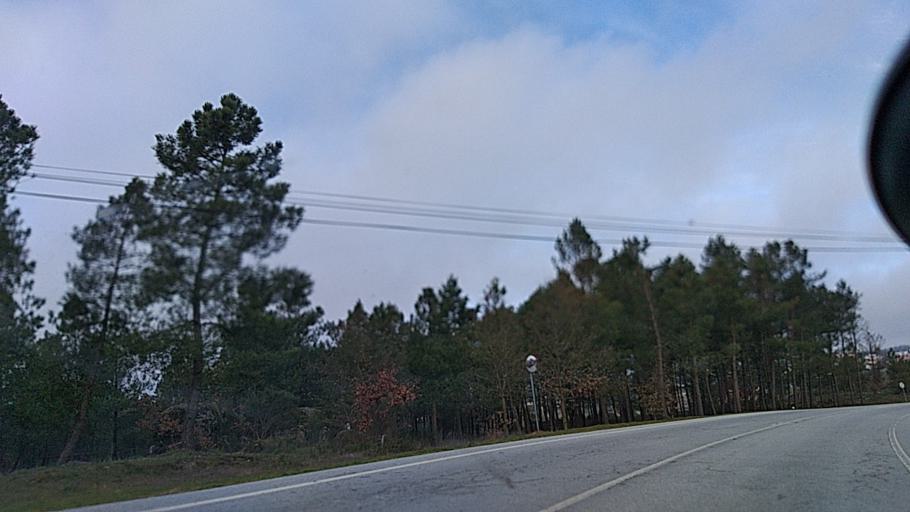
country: PT
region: Guarda
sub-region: Aguiar da Beira
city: Aguiar da Beira
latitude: 40.8087
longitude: -7.5319
